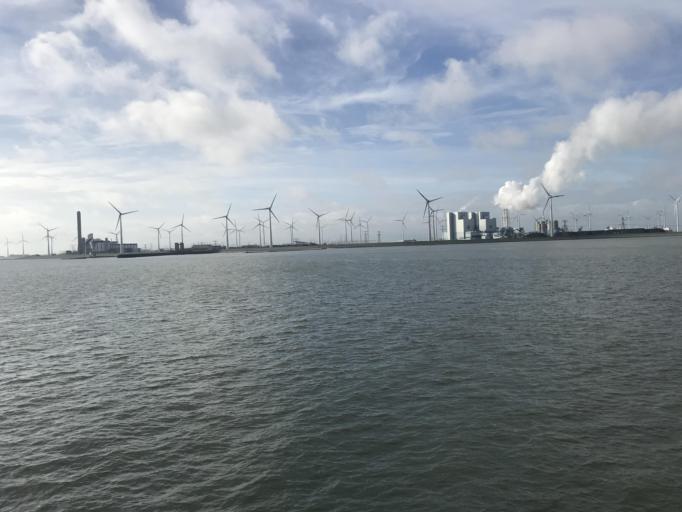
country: NL
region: Groningen
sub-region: Gemeente Delfzijl
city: Delfzijl
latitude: 53.4510
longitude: 6.8900
